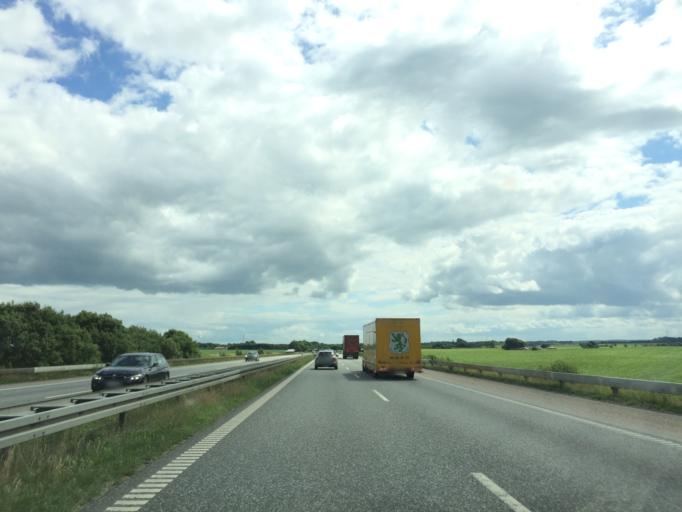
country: DK
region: North Denmark
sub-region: Mariagerfjord Kommune
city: Hobro
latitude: 56.7222
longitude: 9.7177
